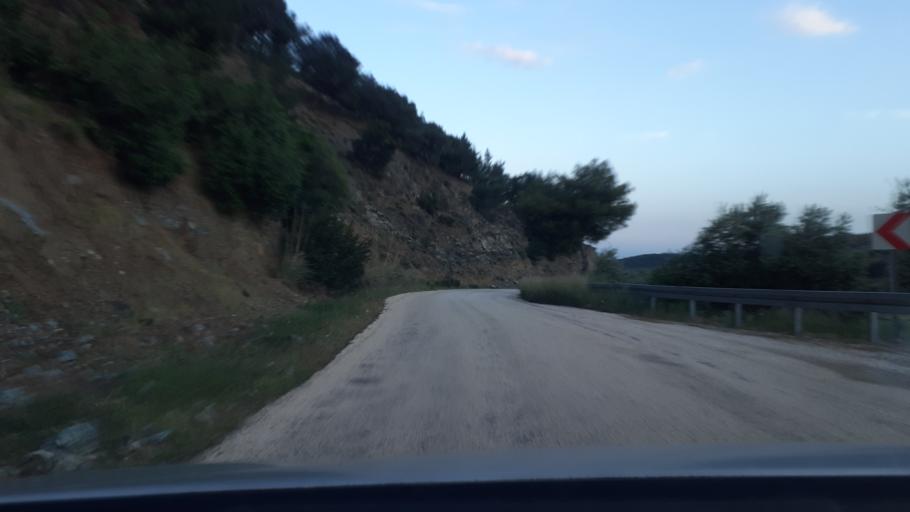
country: TR
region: Hatay
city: Kirikhan
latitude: 36.5176
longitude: 36.3184
